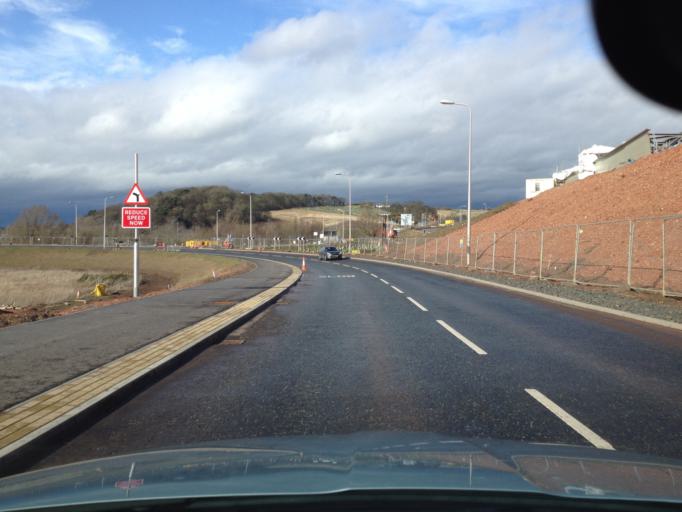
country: GB
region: Scotland
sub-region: Fife
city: North Queensferry
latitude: 56.0175
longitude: -3.4064
